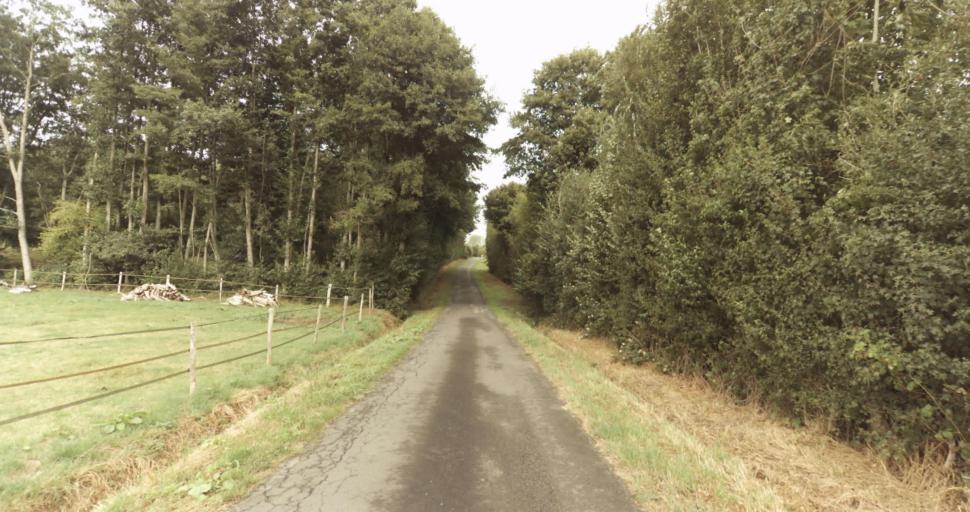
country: FR
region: Lower Normandy
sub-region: Departement de l'Orne
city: Sainte-Gauburge-Sainte-Colombe
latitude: 48.7214
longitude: 0.4811
